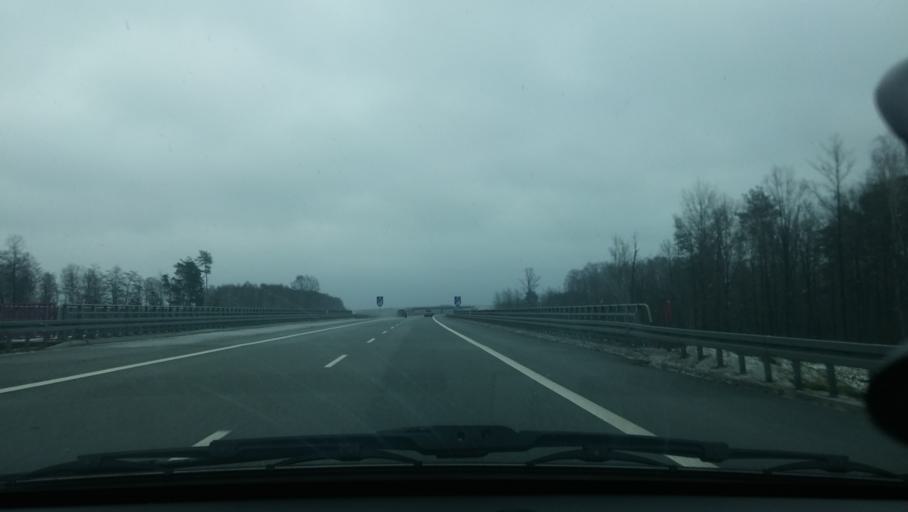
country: PL
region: Masovian Voivodeship
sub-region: Powiat minski
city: Ceglow
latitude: 52.2029
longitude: 21.7431
